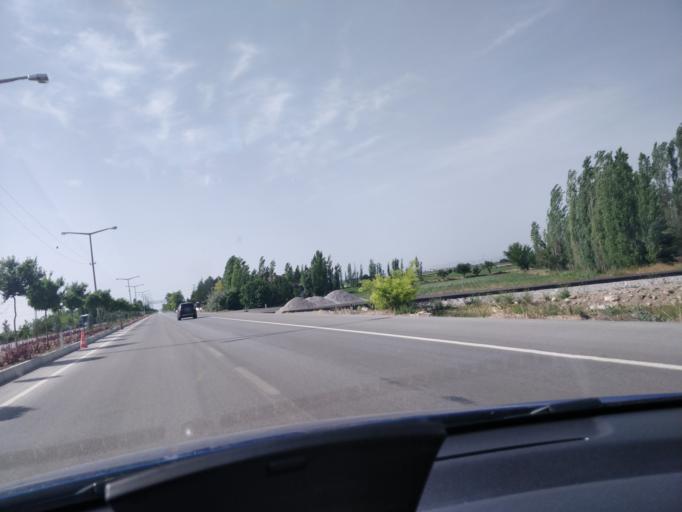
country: TR
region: Konya
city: Cumra
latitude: 37.5633
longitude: 32.6635
